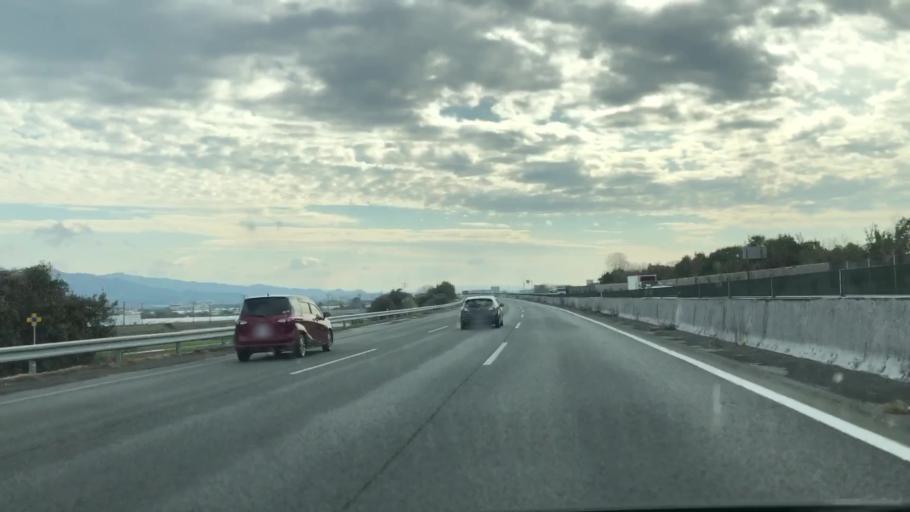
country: JP
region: Saga Prefecture
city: Tosu
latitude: 33.3516
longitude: 130.5377
